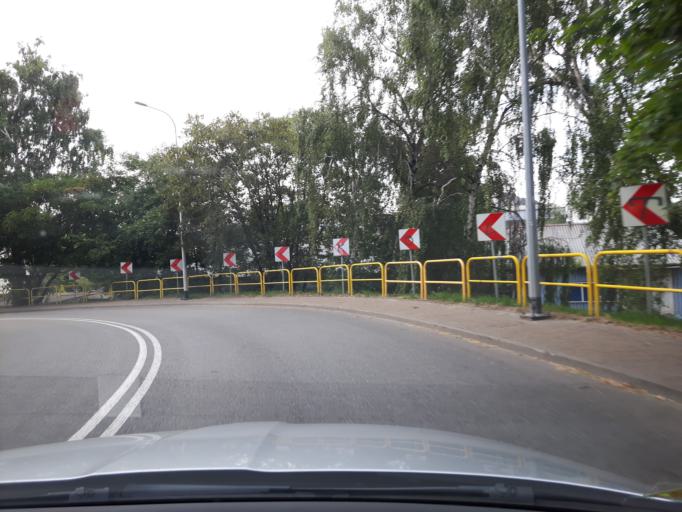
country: PL
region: Pomeranian Voivodeship
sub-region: Gdynia
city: Gdynia
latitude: 54.5287
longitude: 18.5446
